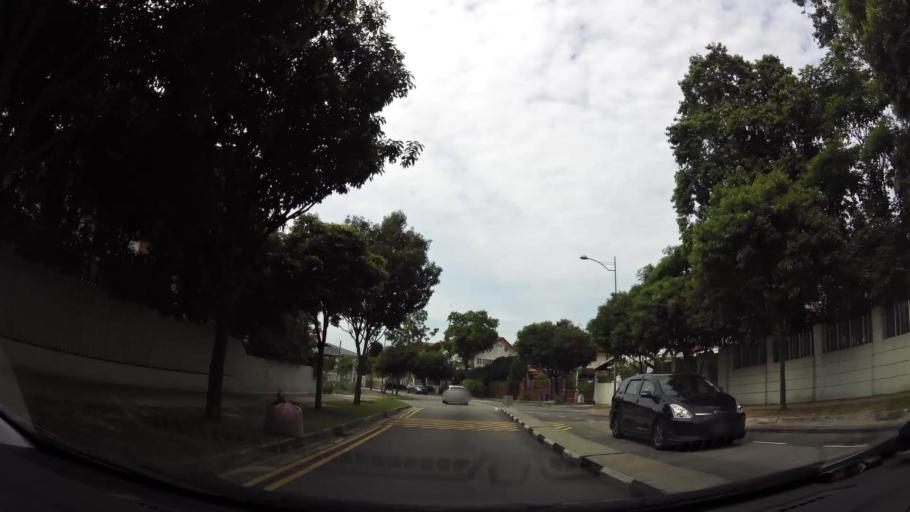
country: SG
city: Singapore
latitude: 1.3169
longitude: 103.7563
